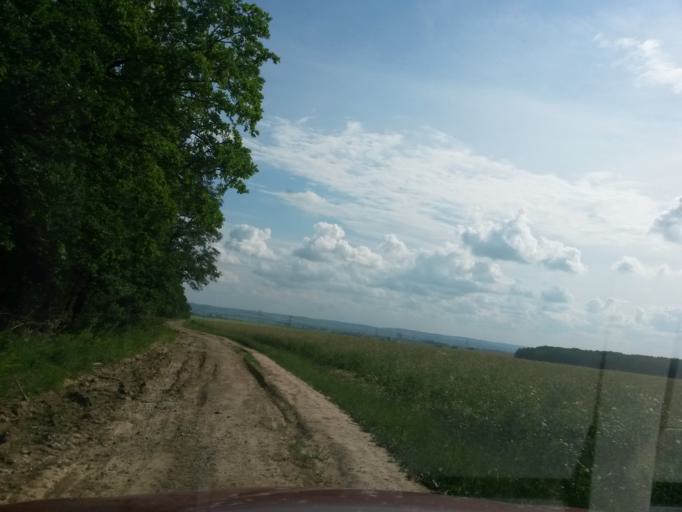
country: SK
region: Kosicky
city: Moldava nad Bodvou
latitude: 48.6191
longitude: 21.1051
